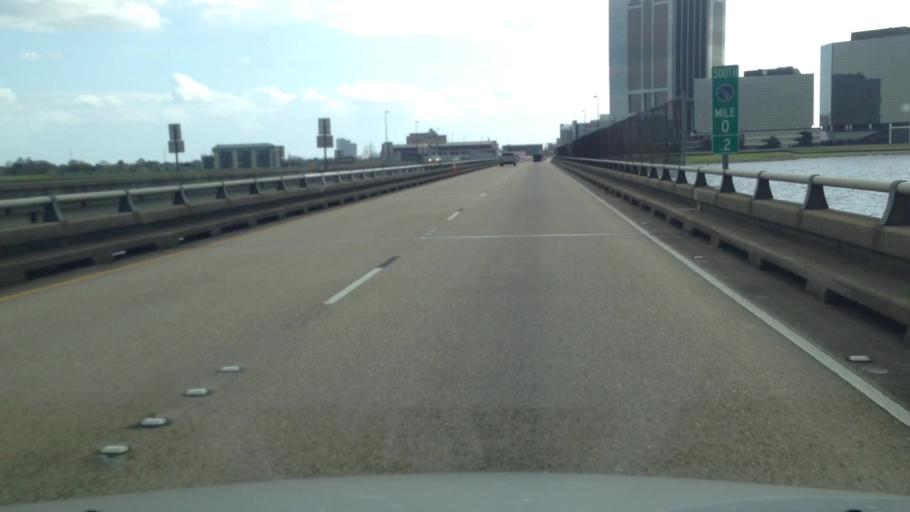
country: US
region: Louisiana
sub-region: Jefferson Parish
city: Metairie
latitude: 30.0247
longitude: -90.1536
